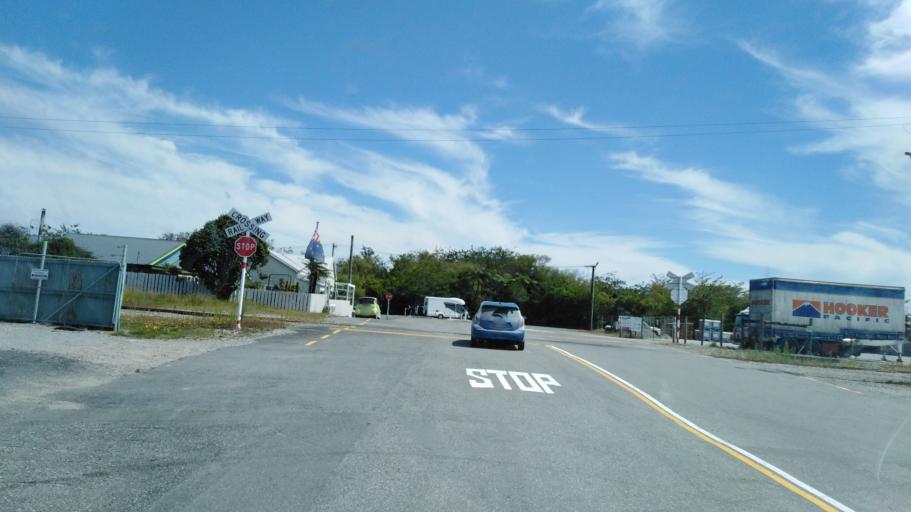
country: NZ
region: West Coast
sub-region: Buller District
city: Westport
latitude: -41.7586
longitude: 171.5983
